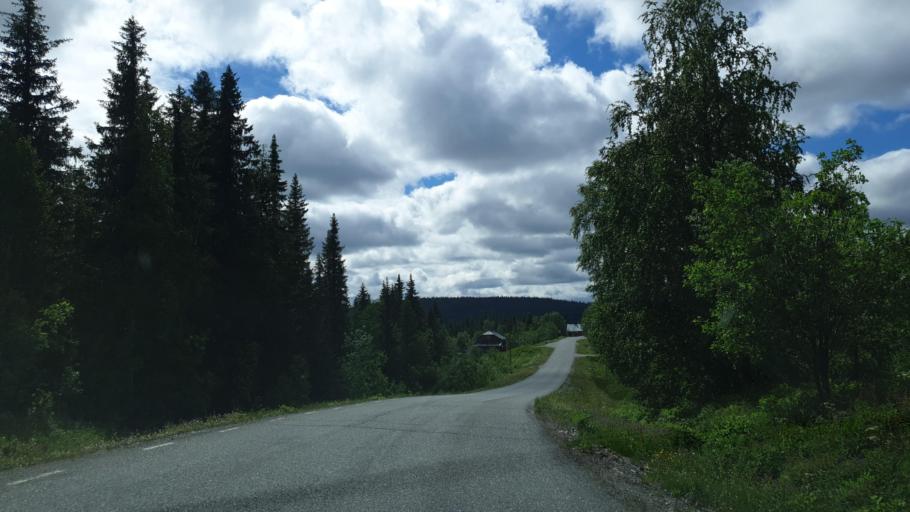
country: SE
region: Vaesterbotten
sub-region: Vilhelmina Kommun
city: Sjoberg
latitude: 65.1957
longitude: 15.9790
